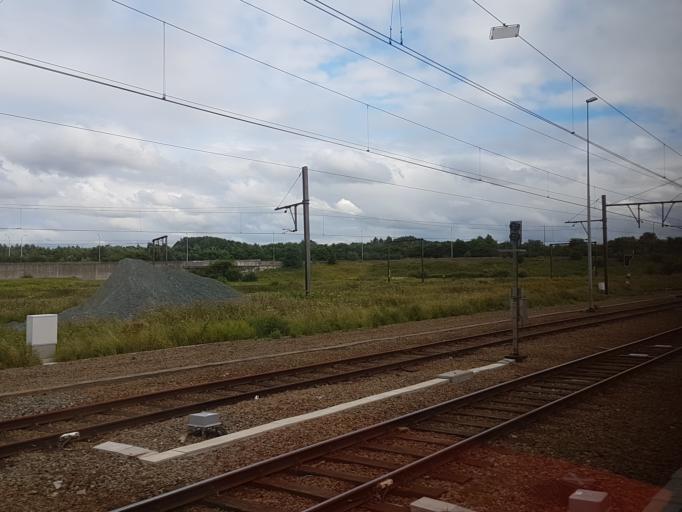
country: BE
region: Flanders
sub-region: Provincie Antwerpen
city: Kapellen
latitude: 51.2667
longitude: 4.4295
